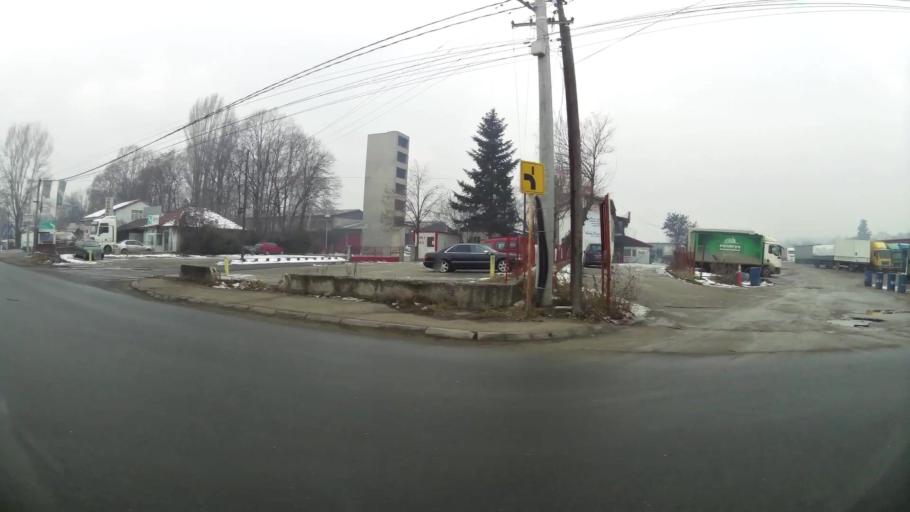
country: MK
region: Cair
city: Cair
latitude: 41.9992
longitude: 21.4601
